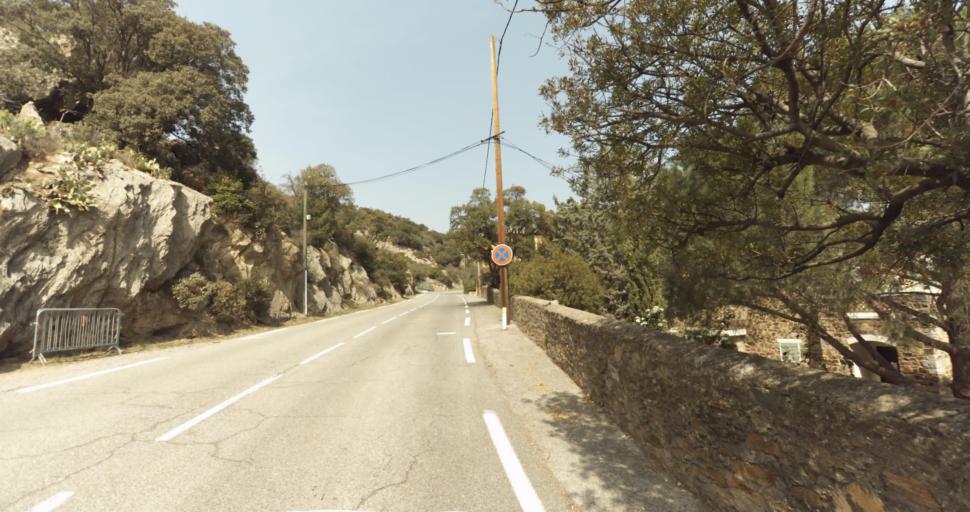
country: FR
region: Provence-Alpes-Cote d'Azur
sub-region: Departement du Var
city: Bormes-les-Mimosas
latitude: 43.1532
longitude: 6.3452
